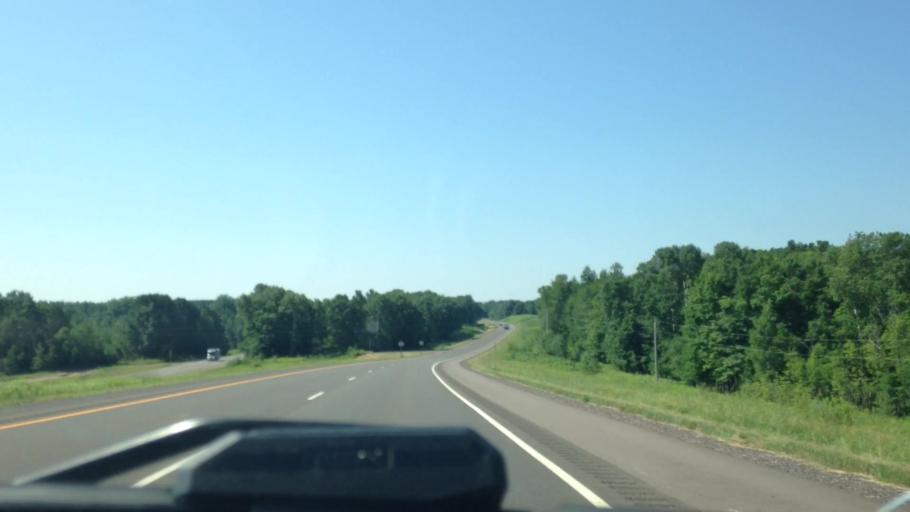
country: US
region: Wisconsin
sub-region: Washburn County
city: Spooner
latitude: 45.9519
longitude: -91.8283
